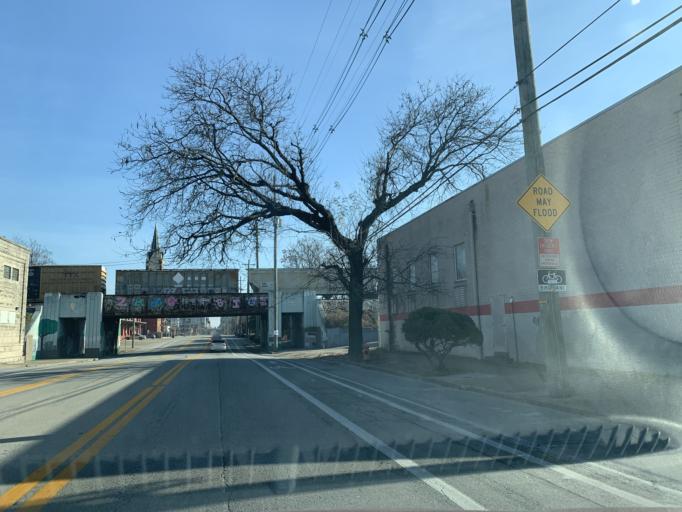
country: US
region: Kentucky
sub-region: Jefferson County
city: Louisville
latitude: 38.2571
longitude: -85.7742
